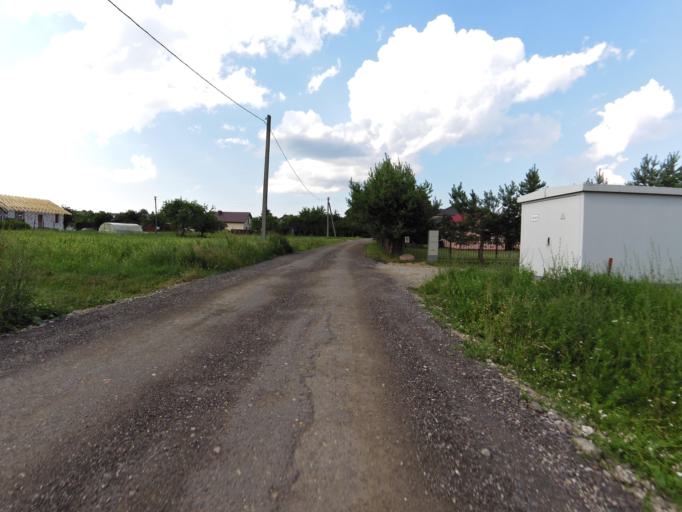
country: LT
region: Vilnius County
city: Pasilaiciai
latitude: 54.7598
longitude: 25.2300
